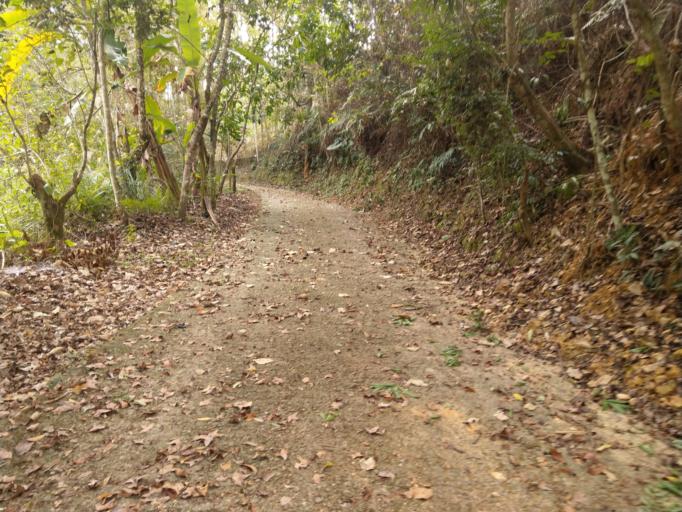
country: TW
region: Taiwan
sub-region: Nantou
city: Puli
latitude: 23.9193
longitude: 120.9220
